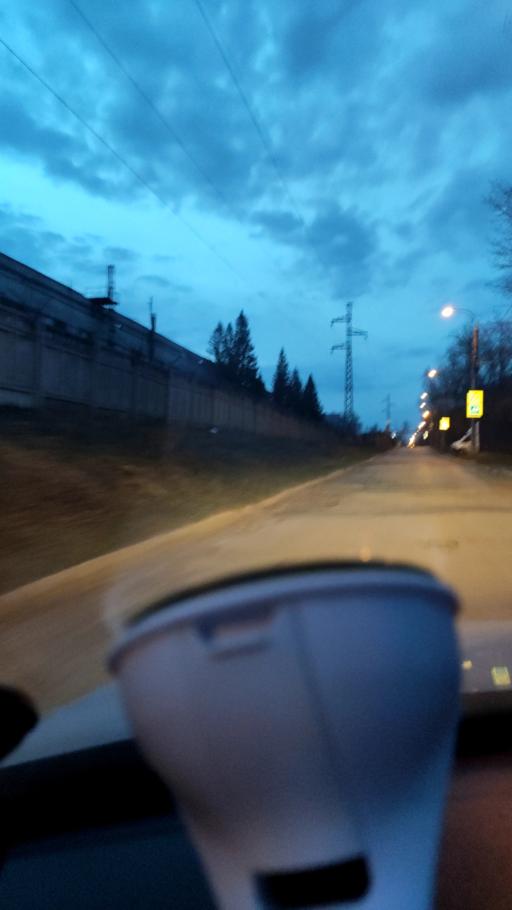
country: RU
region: Samara
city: Volzhskiy
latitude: 53.3468
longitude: 50.2088
